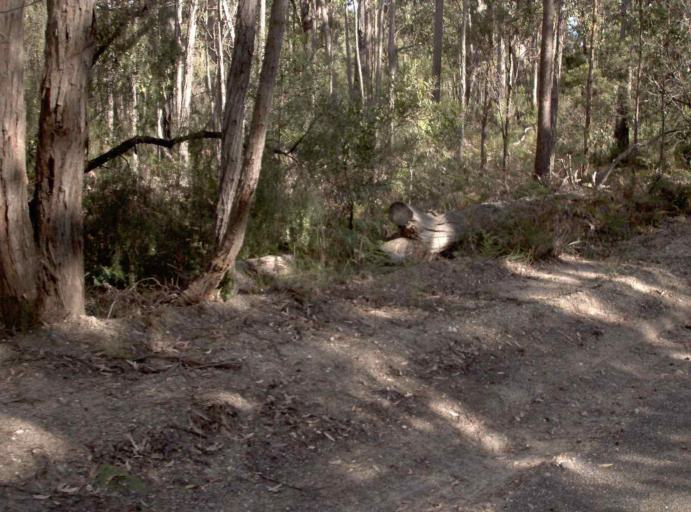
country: AU
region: Victoria
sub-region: East Gippsland
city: Lakes Entrance
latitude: -37.6813
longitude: 148.0533
